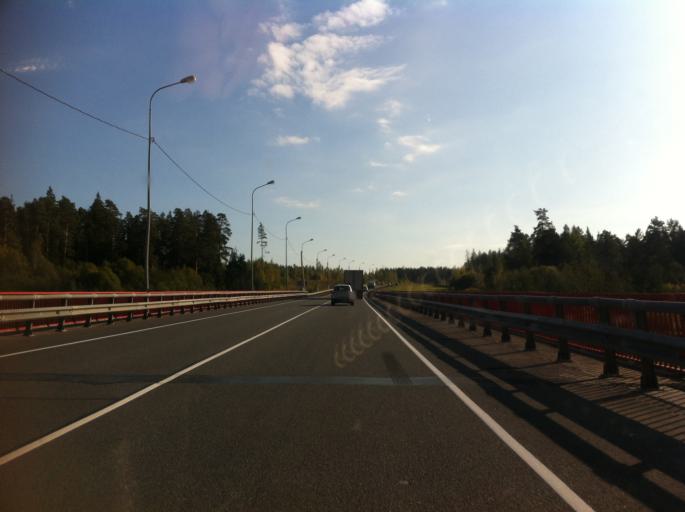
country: RU
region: Leningrad
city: Luga
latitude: 58.7531
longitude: 29.8921
